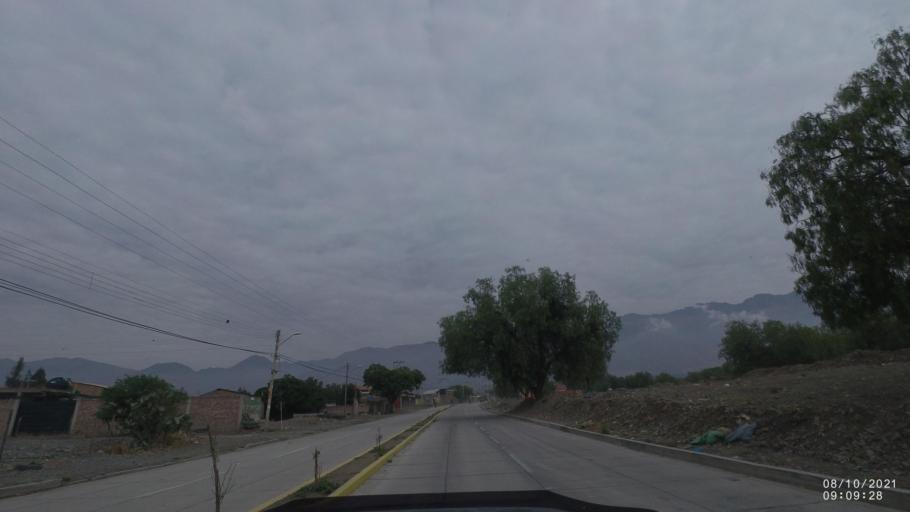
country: BO
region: Cochabamba
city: Sipe Sipe
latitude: -17.3961
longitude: -66.3274
